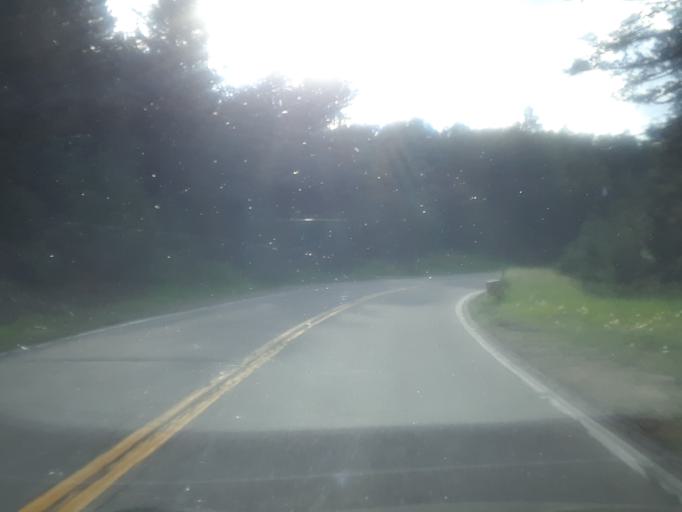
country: US
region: Colorado
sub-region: Jefferson County
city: Kittredge
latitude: 39.7166
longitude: -105.3647
